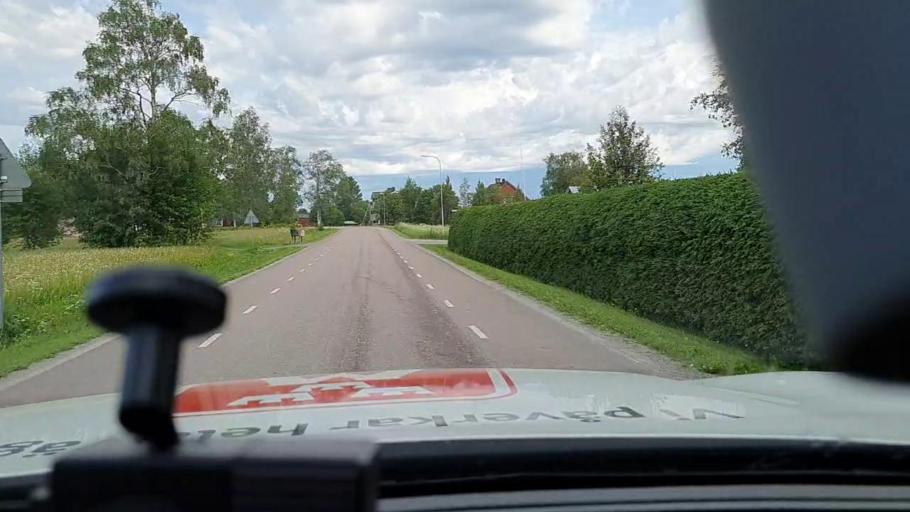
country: SE
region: Norrbotten
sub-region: Bodens Kommun
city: Saevast
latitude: 65.6827
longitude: 21.7991
